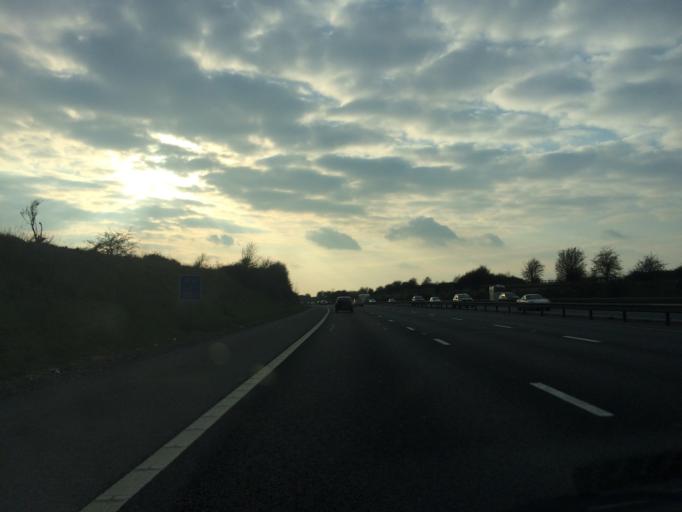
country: GB
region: England
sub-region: Borough of Swindon
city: Wanborough
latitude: 51.5266
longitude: -1.6807
